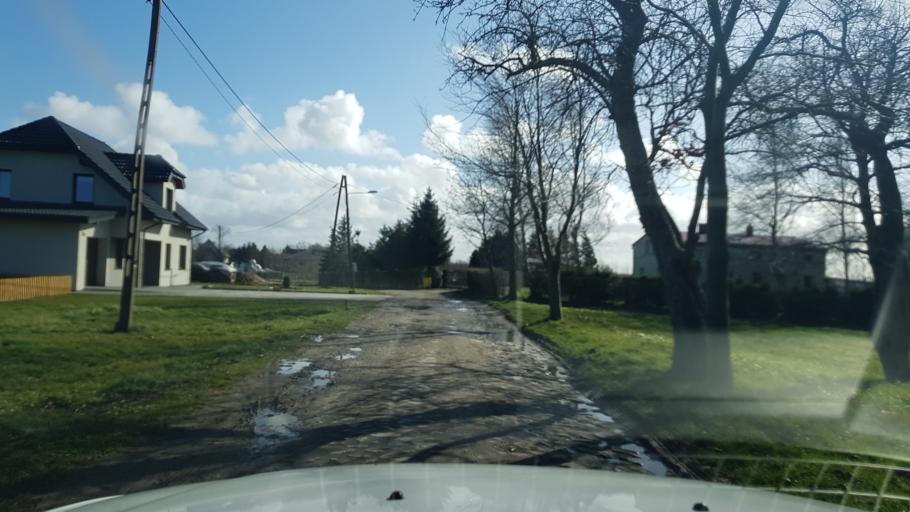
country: PL
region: West Pomeranian Voivodeship
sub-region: Powiat slawienski
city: Slawno
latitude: 54.3660
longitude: 16.5788
